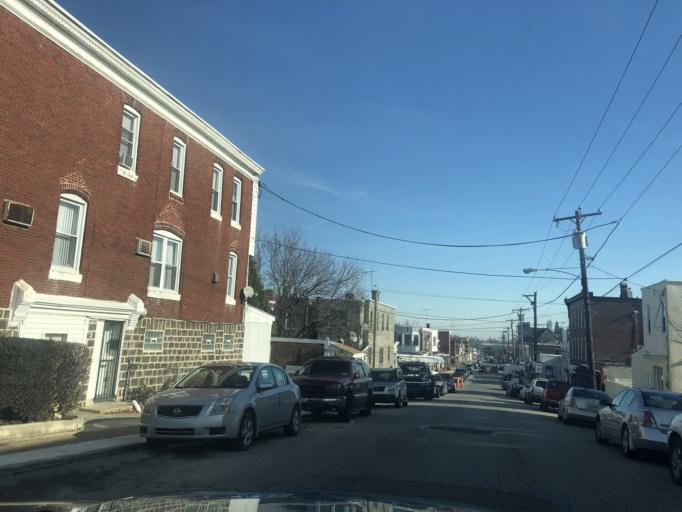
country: US
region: Pennsylvania
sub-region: Delaware County
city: Millbourne
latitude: 39.9707
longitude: -75.2481
